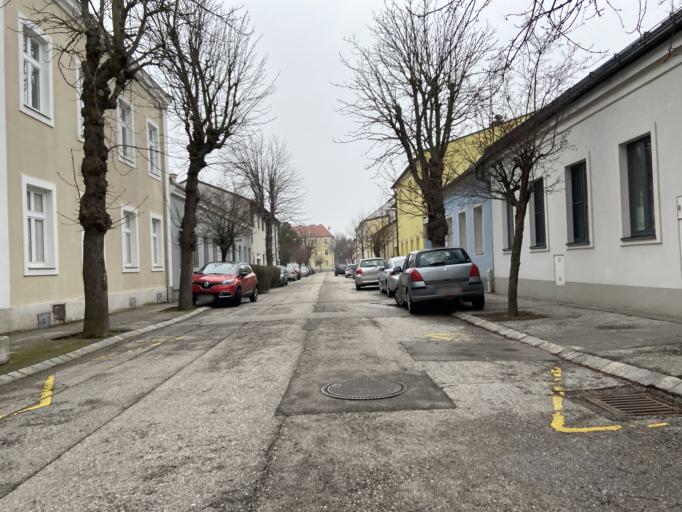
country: AT
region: Lower Austria
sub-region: Politischer Bezirk Modling
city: Guntramsdorf
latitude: 48.0461
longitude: 16.3104
